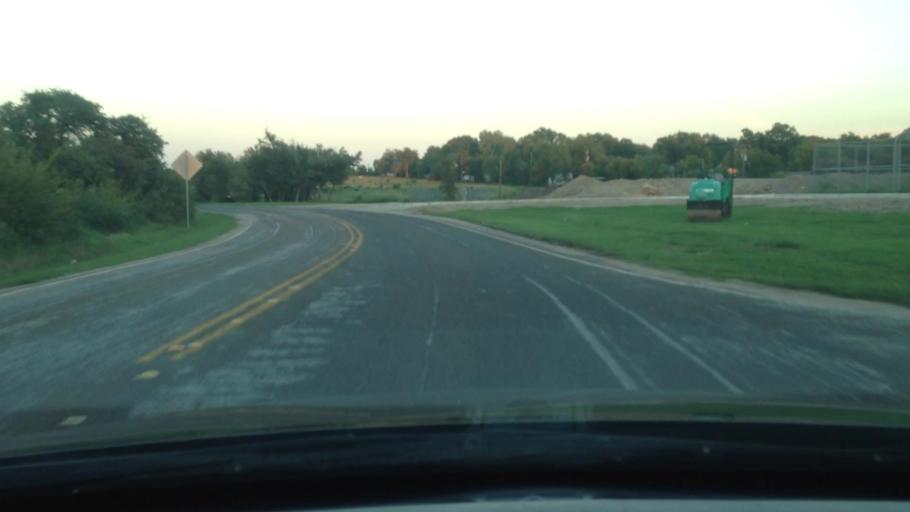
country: US
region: Texas
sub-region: Tarrant County
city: White Settlement
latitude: 32.7783
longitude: -97.4672
